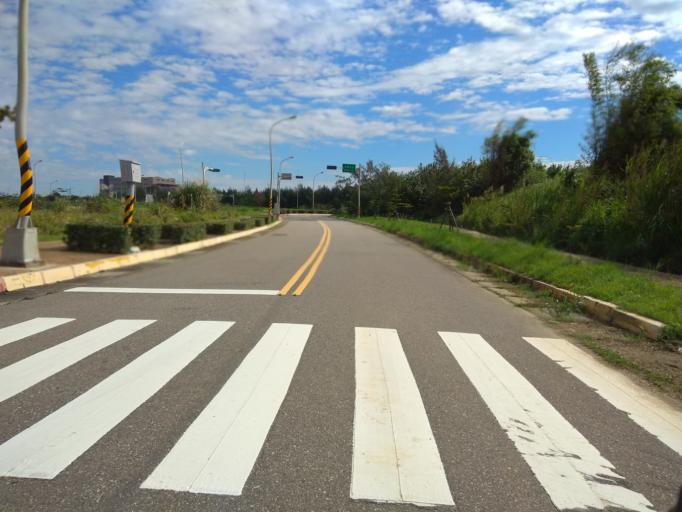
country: TW
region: Taiwan
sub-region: Hsinchu
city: Zhubei
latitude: 25.0446
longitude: 121.0827
